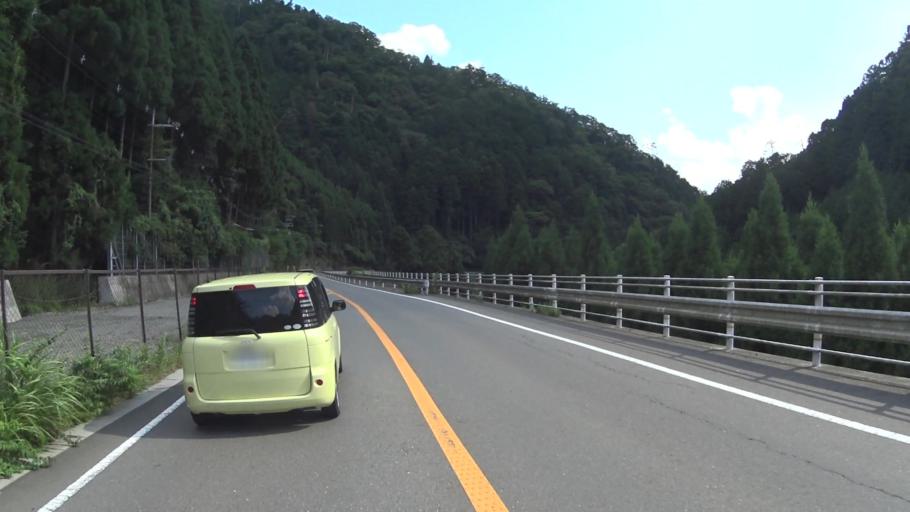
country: JP
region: Kyoto
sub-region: Kyoto-shi
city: Kamigyo-ku
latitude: 35.0731
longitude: 135.6853
